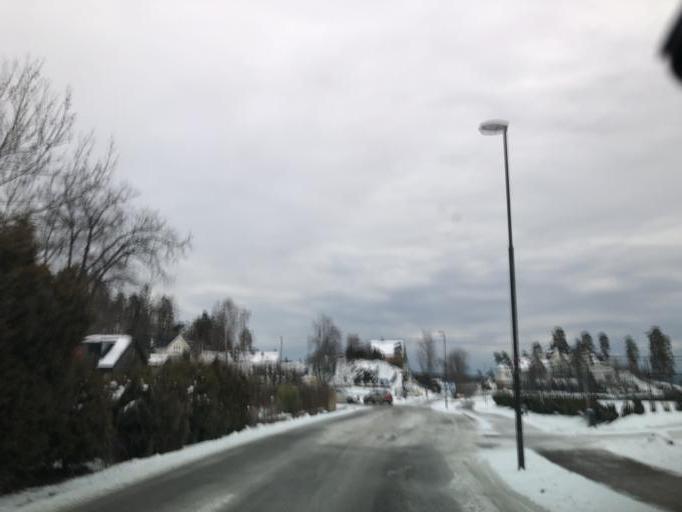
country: NO
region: Akershus
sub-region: Baerum
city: Sandvika
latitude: 59.8600
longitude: 10.5167
